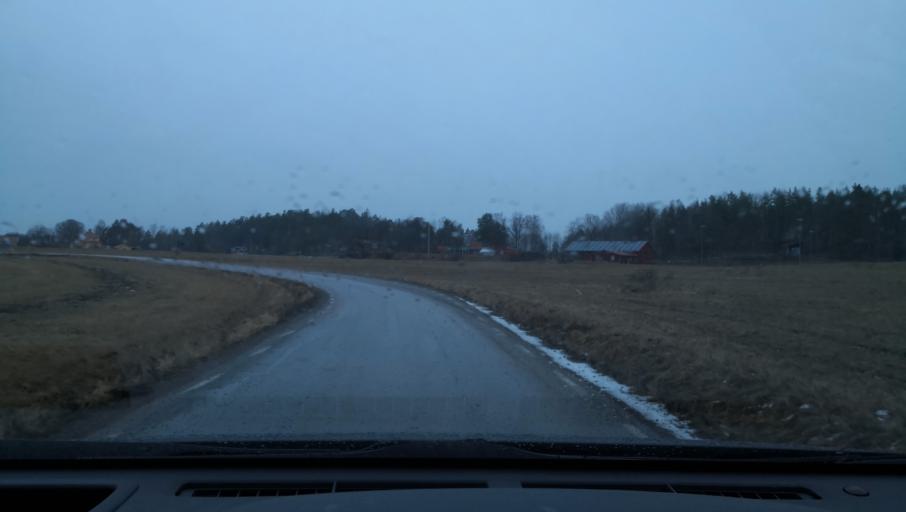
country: SE
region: Soedermanland
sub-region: Eskilstuna Kommun
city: Arla
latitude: 59.4521
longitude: 16.7367
